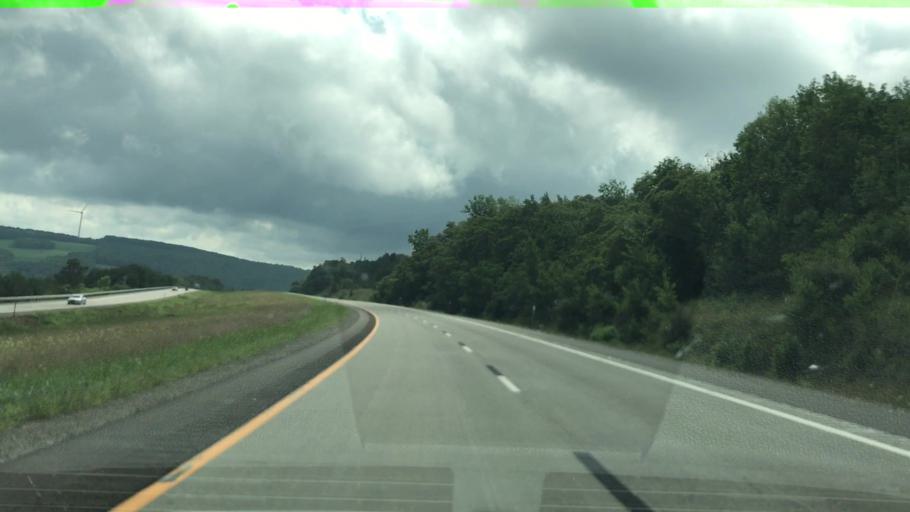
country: US
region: New York
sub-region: Steuben County
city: Wayland
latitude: 42.5143
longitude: -77.5348
